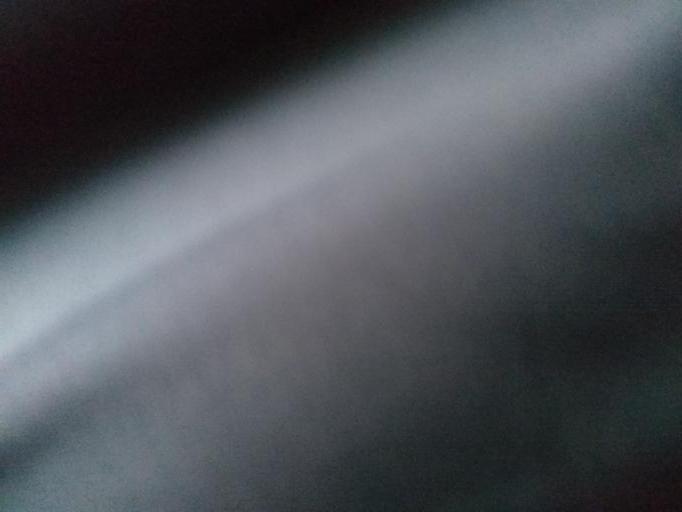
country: BD
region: Dhaka
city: Azimpur
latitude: 23.7725
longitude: 90.3818
